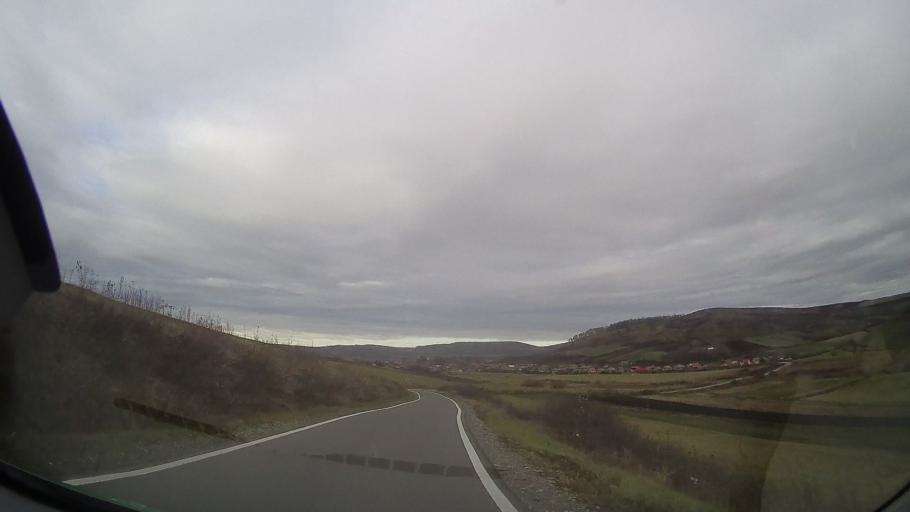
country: RO
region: Mures
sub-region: Comuna Faragau
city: Faragau
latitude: 46.7711
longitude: 24.5566
